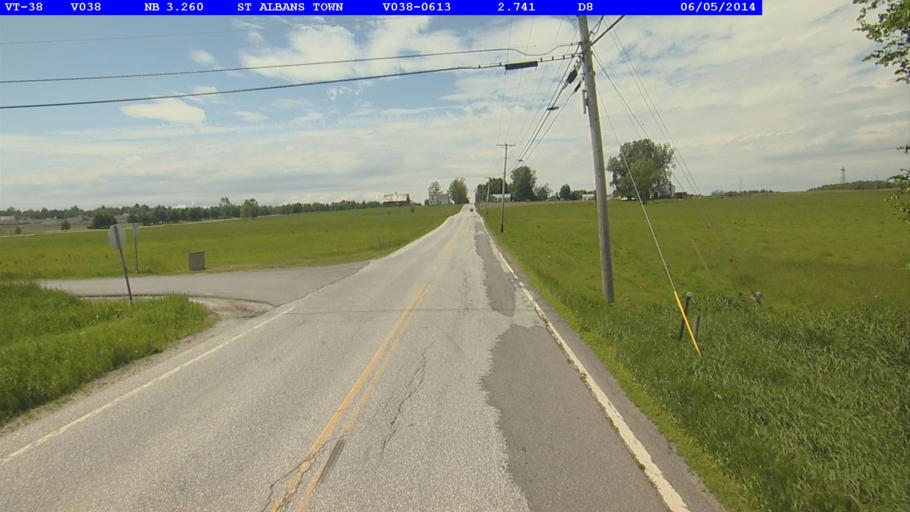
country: US
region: Vermont
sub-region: Franklin County
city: Saint Albans
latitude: 44.8516
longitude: -73.1265
